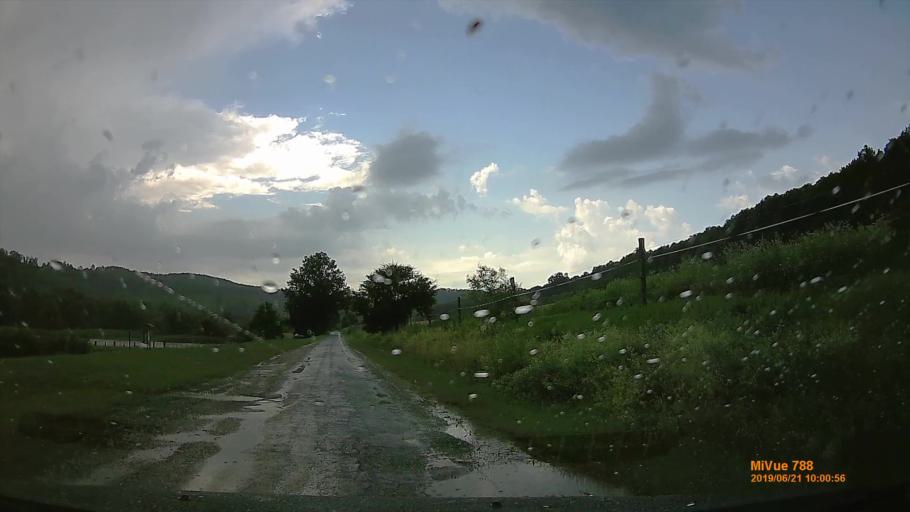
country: HU
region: Baranya
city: Buekkoesd
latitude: 46.2062
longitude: 17.9725
